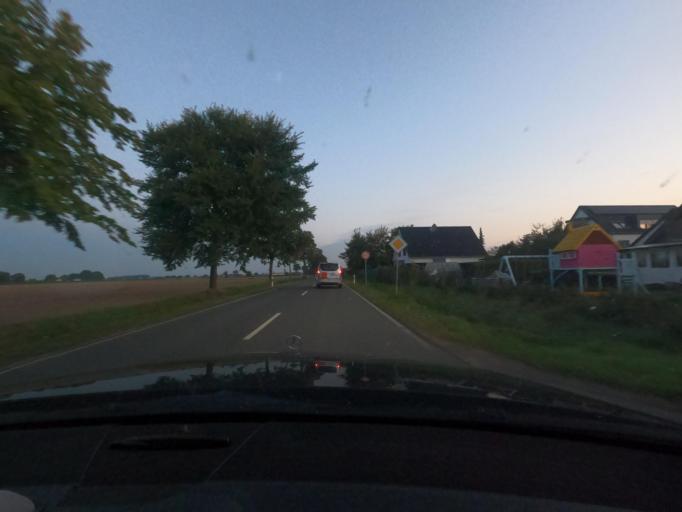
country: DE
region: North Rhine-Westphalia
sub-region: Regierungsbezirk Detmold
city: Salzkotten
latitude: 51.6529
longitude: 8.5939
